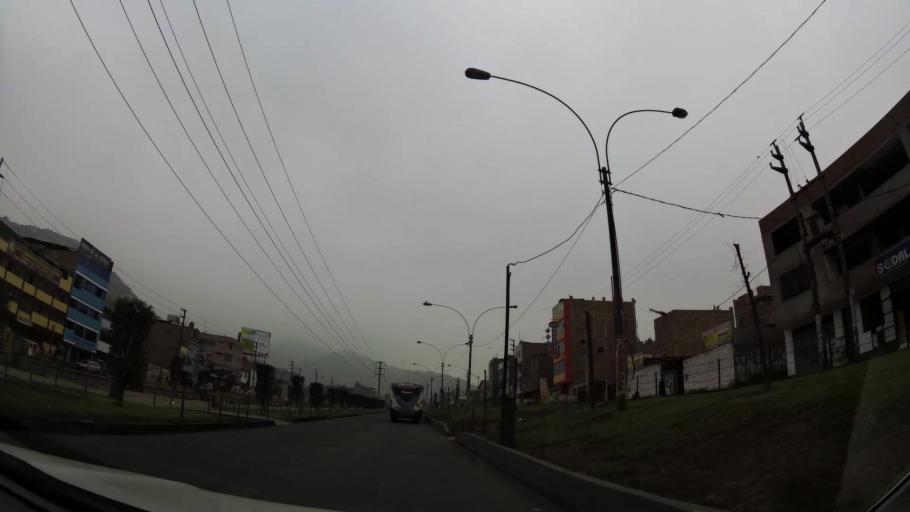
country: PE
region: Lima
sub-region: Lima
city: Independencia
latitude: -11.9423
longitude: -76.9812
